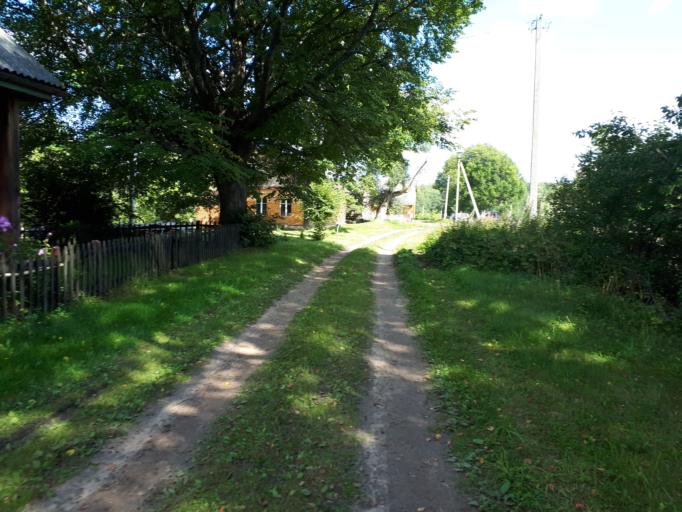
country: BY
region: Vitebsk
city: Rasony
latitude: 55.9891
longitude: 28.6012
